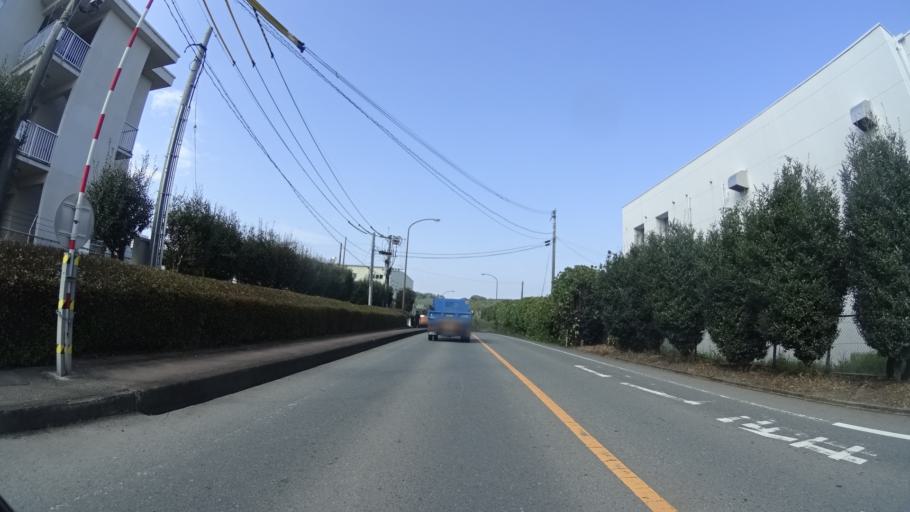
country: JP
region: Kumamoto
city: Ozu
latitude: 32.8331
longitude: 130.8562
